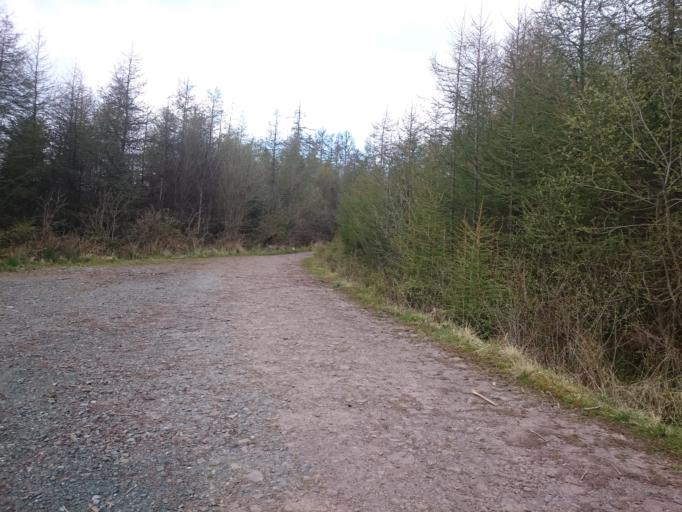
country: GB
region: Scotland
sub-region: Stirling
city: Killearn
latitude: 56.0895
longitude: -4.4834
